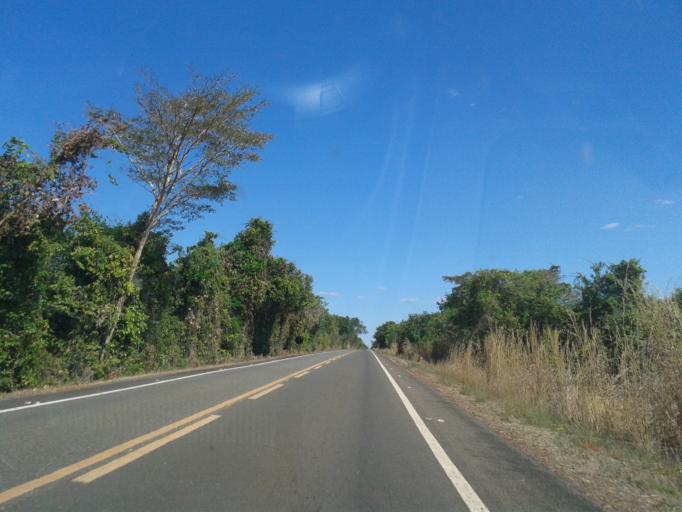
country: BR
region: Goias
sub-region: Sao Miguel Do Araguaia
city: Sao Miguel do Araguaia
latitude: -13.7144
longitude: -50.3335
